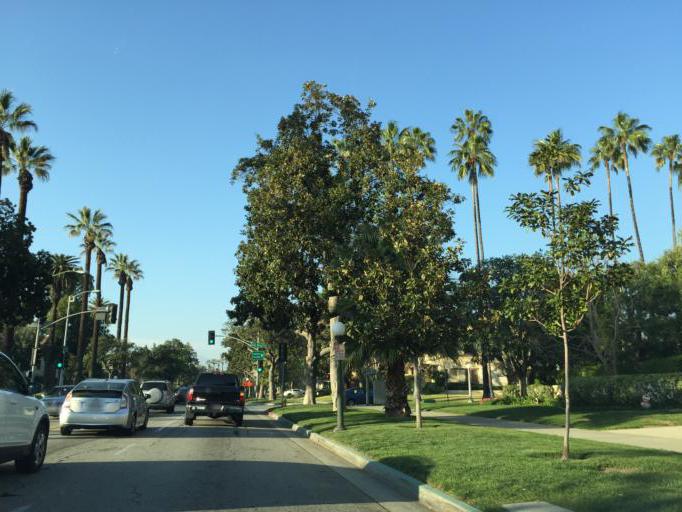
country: US
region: California
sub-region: Los Angeles County
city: Pasadena
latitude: 34.1402
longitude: -118.1594
